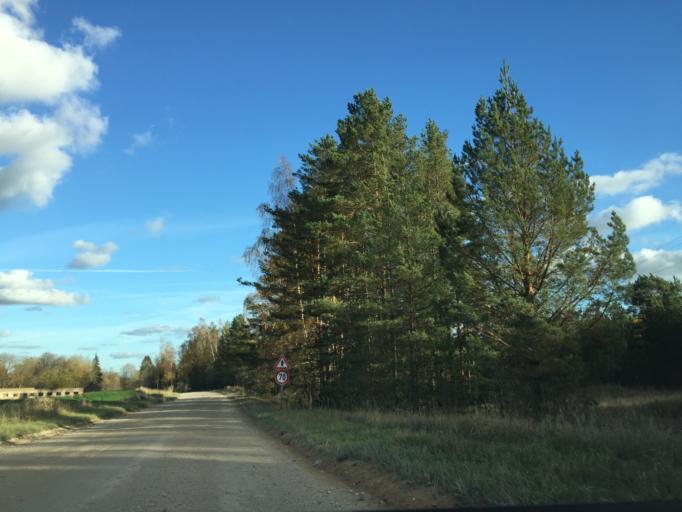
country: LV
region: Tukuma Rajons
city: Tukums
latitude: 56.9601
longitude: 23.0117
